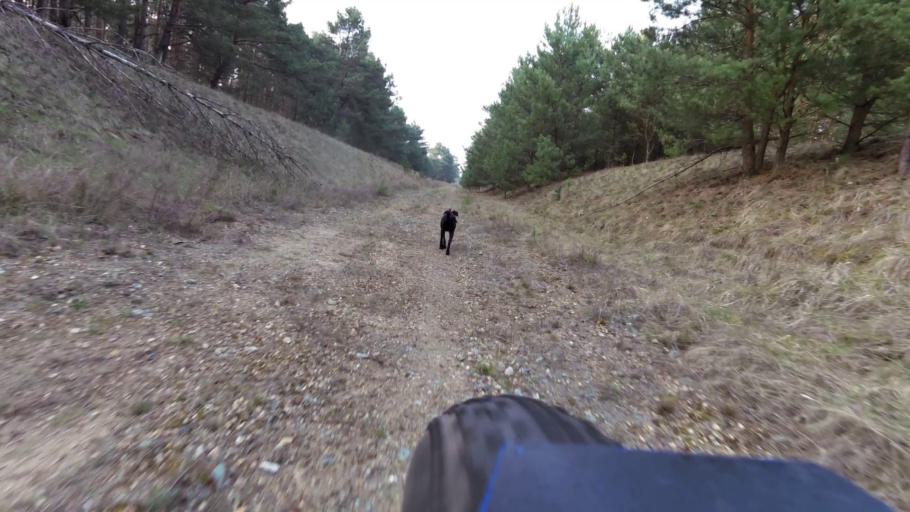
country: DE
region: Brandenburg
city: Vogelsang
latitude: 52.2634
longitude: 14.6920
